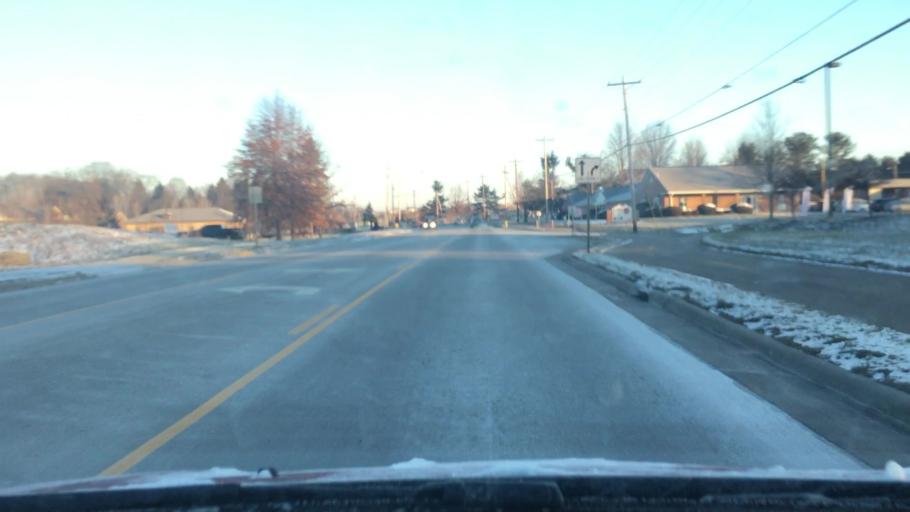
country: US
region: Ohio
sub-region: Wayne County
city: Wooster
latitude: 40.8222
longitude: -81.9079
